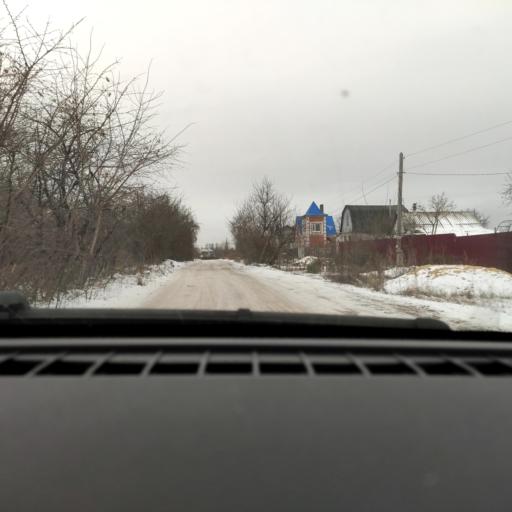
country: RU
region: Voronezj
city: Maslovka
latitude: 51.6028
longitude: 39.2805
